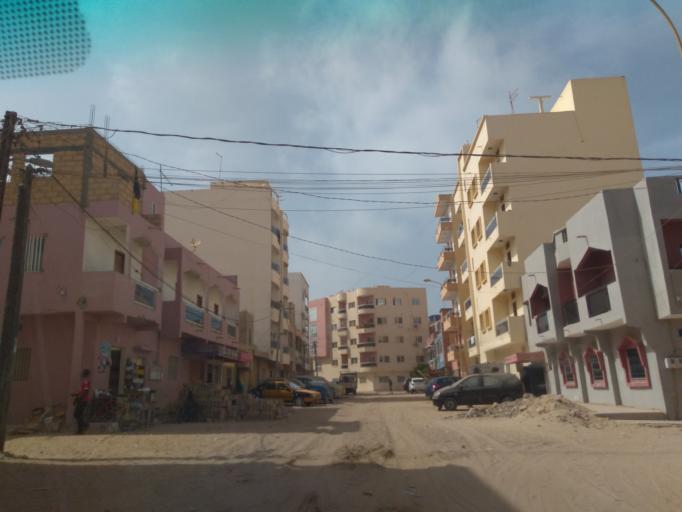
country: SN
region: Dakar
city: Grand Dakar
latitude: 14.7601
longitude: -17.4660
